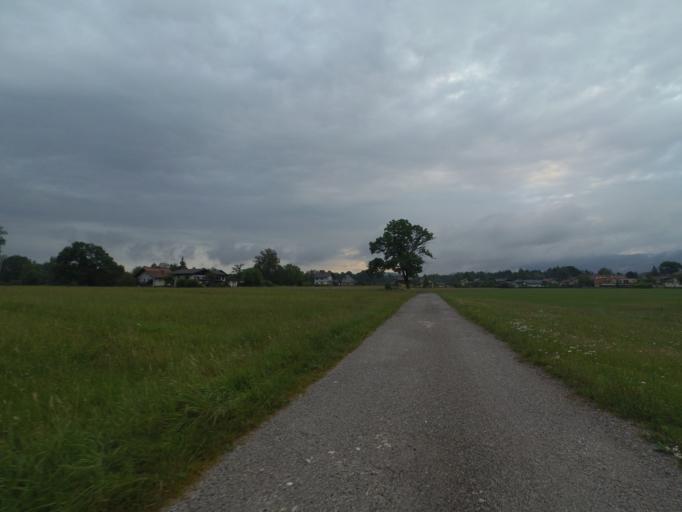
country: AT
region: Salzburg
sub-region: Politischer Bezirk Salzburg-Umgebung
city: Grodig
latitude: 47.7594
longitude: 13.0299
